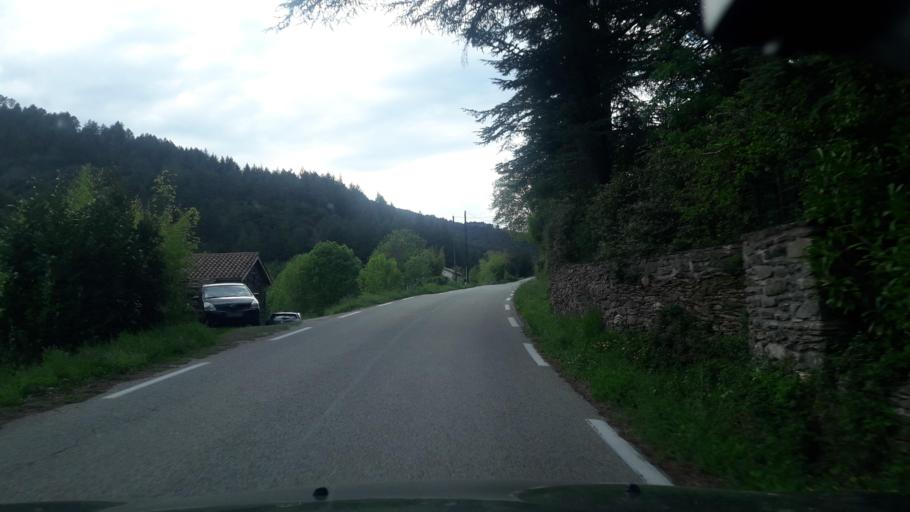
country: FR
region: Languedoc-Roussillon
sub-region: Departement du Gard
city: Valleraugue
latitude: 44.1396
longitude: 3.7054
